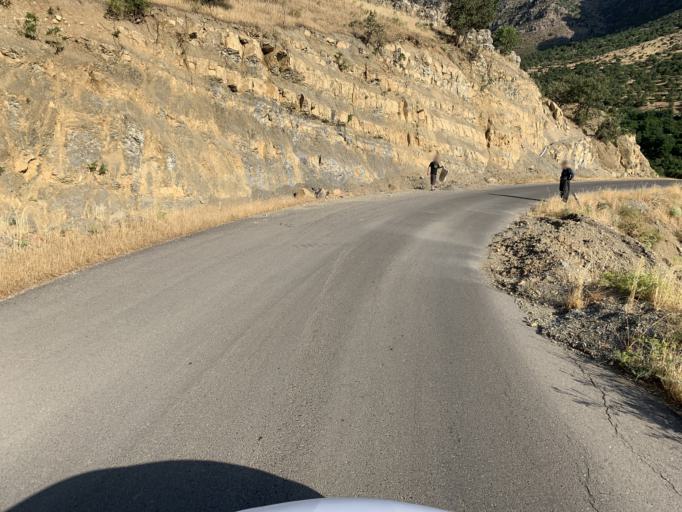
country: IQ
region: As Sulaymaniyah
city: Qeladize
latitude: 35.9938
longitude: 45.1950
